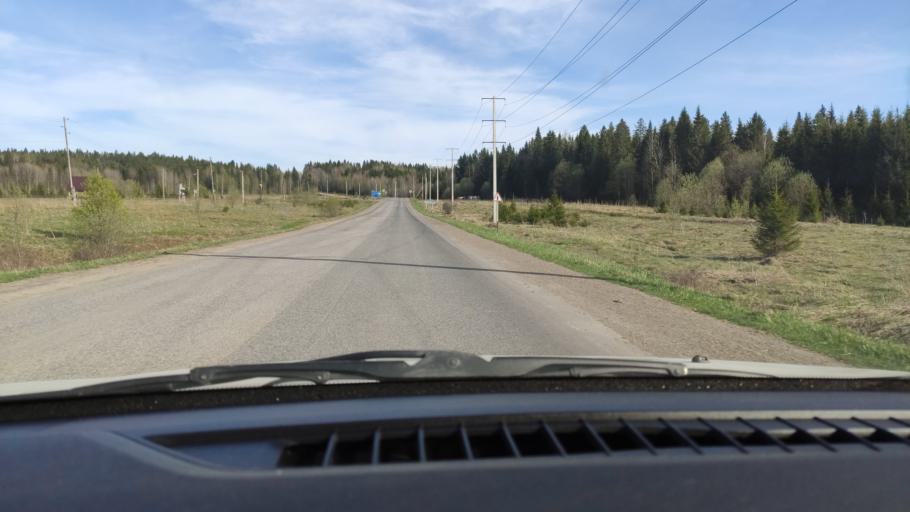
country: RU
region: Perm
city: Novyye Lyady
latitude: 57.9322
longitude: 56.6380
